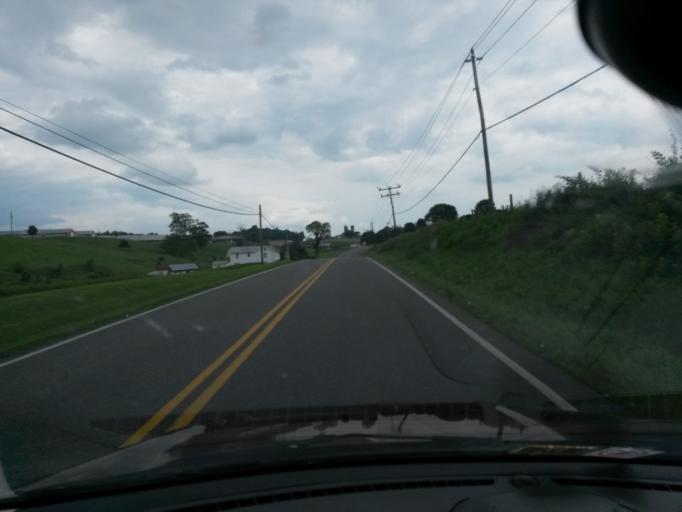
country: US
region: Virginia
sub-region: Rockingham County
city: Dayton
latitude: 38.4645
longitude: -78.9663
